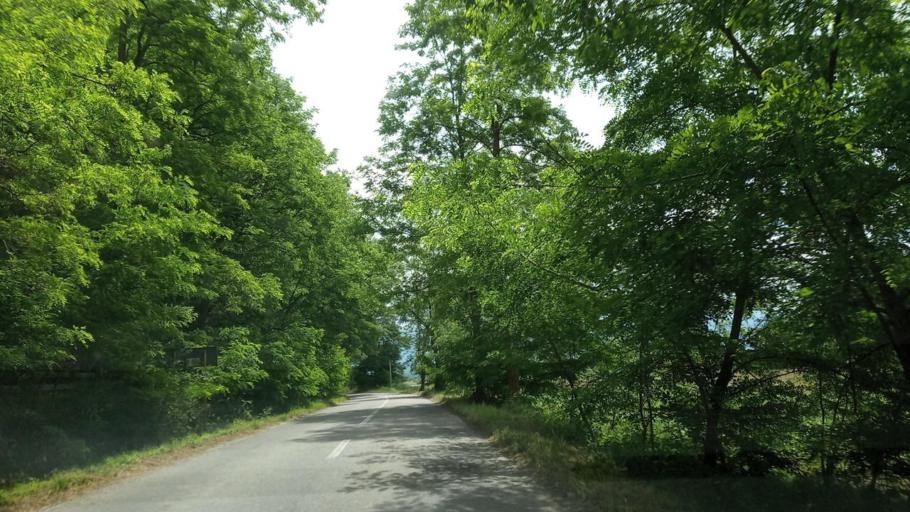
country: RO
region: Sibiu
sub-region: Comuna Porumbacu de Jos
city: Porumbacu de Jos
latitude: 45.7325
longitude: 24.4694
